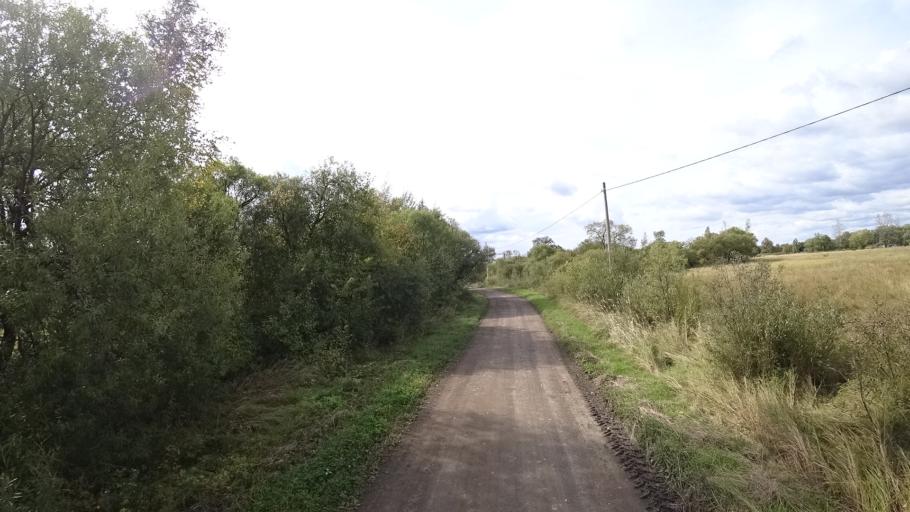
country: RU
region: Amur
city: Arkhara
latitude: 49.3479
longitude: 130.1637
